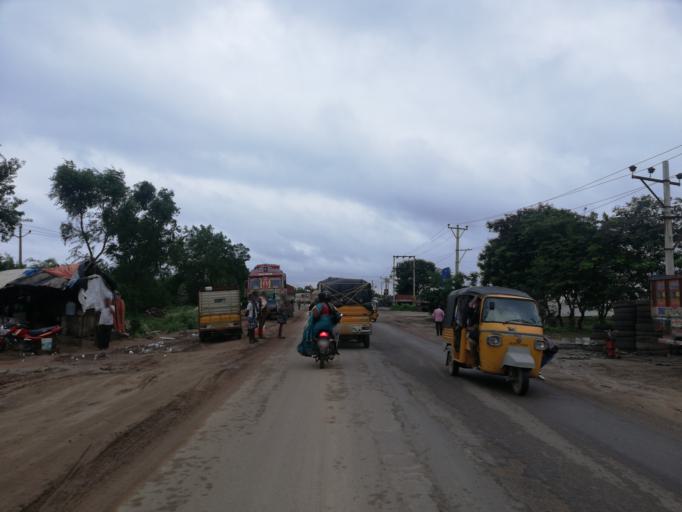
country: IN
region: Telangana
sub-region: Rangareddi
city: Quthbullapur
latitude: 17.5724
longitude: 78.4206
